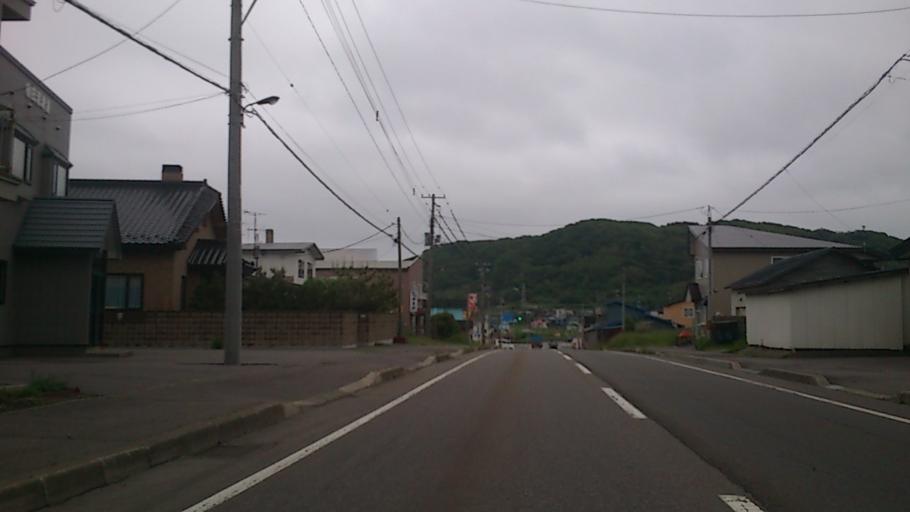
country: JP
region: Hokkaido
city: Kamiiso
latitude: 41.9758
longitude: 140.1366
